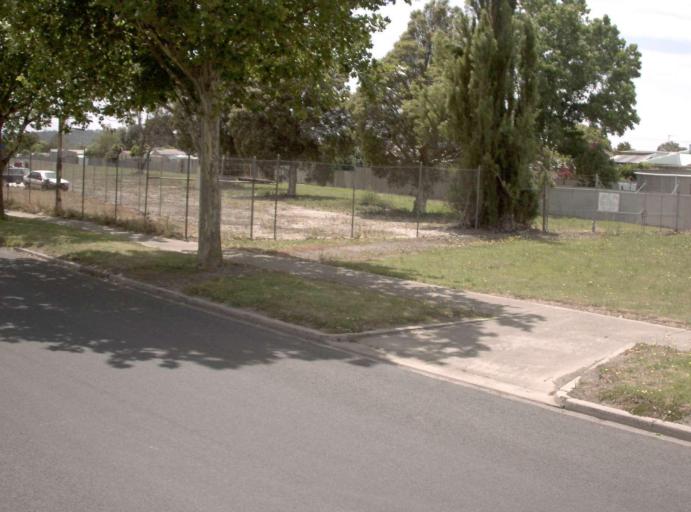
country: AU
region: Victoria
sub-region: Latrobe
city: Moe
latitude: -38.1660
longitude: 146.2630
